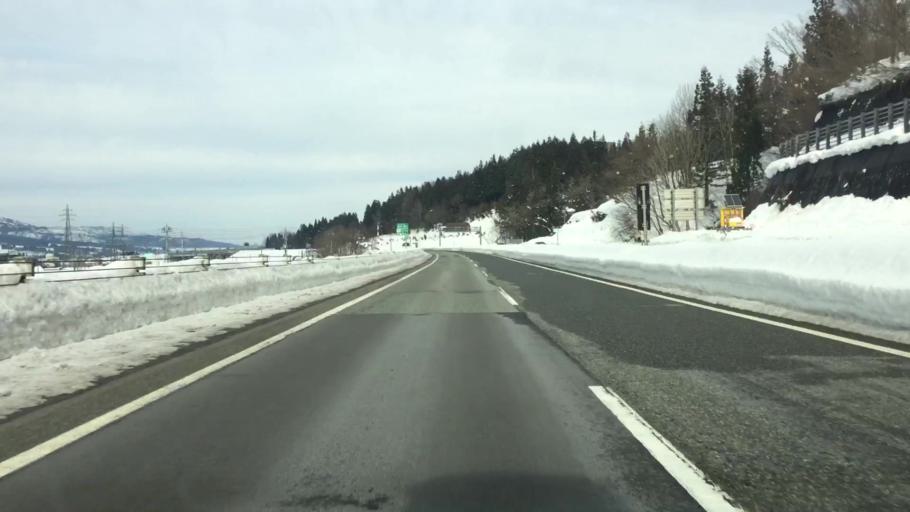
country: JP
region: Niigata
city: Shiozawa
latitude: 36.9836
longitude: 138.8143
